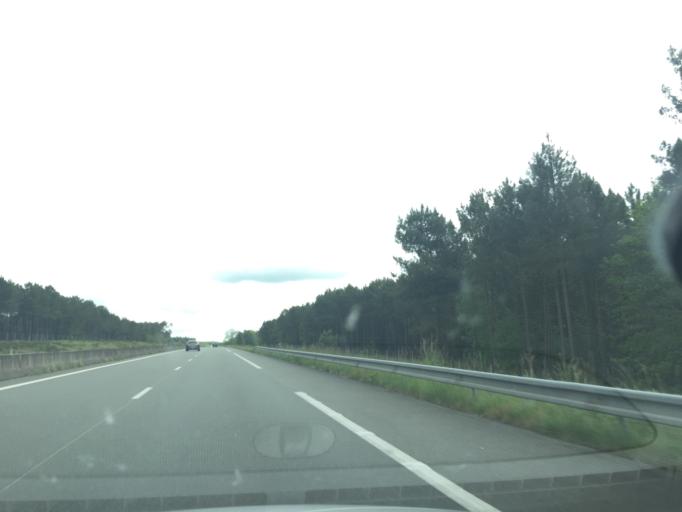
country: FR
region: Pays de la Loire
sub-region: Departement de la Sarthe
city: Mayet
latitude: 47.7324
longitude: 0.3287
